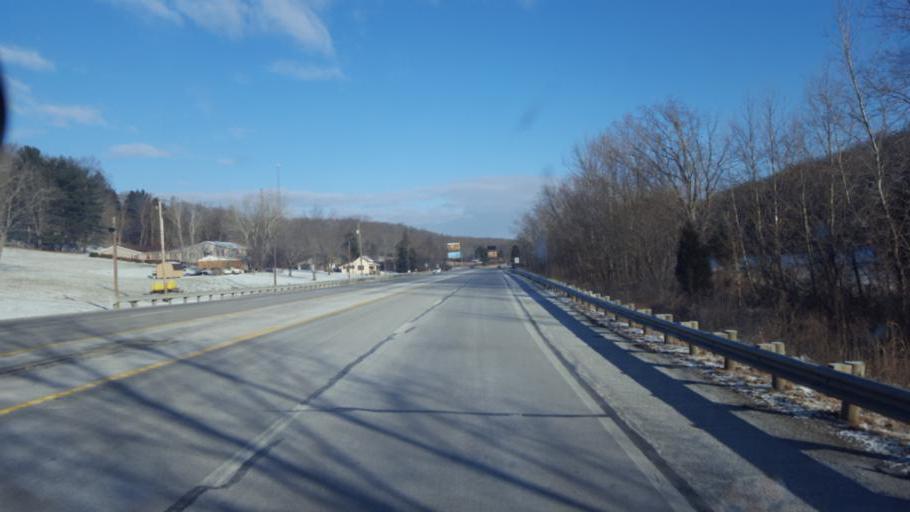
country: US
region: Ohio
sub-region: Ross County
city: Chillicothe
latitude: 39.2320
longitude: -82.9843
